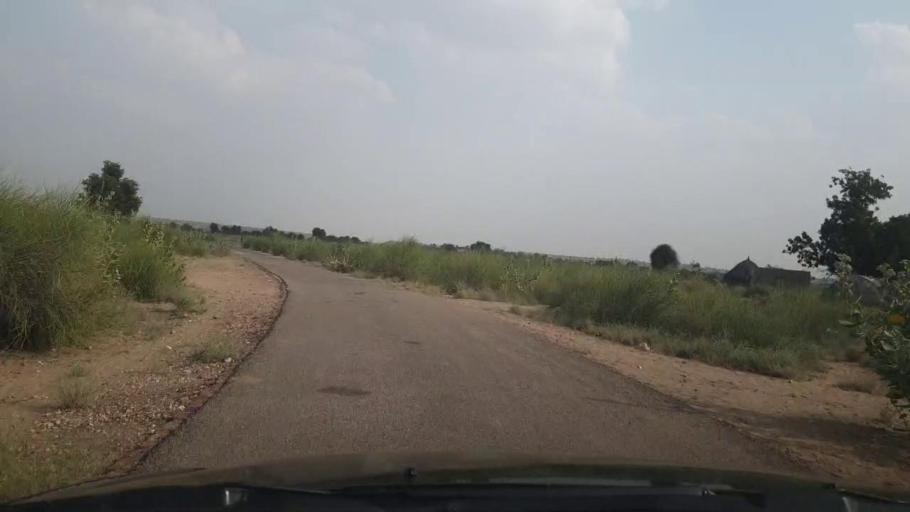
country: PK
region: Sindh
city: Islamkot
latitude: 25.0128
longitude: 70.5937
